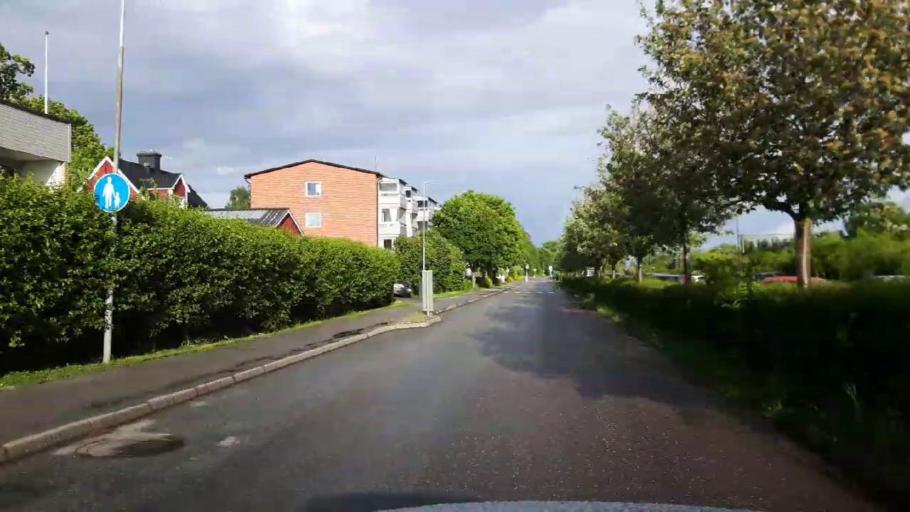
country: SE
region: Stockholm
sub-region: Upplands-Bro Kommun
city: Bro
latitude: 59.5114
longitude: 17.6372
